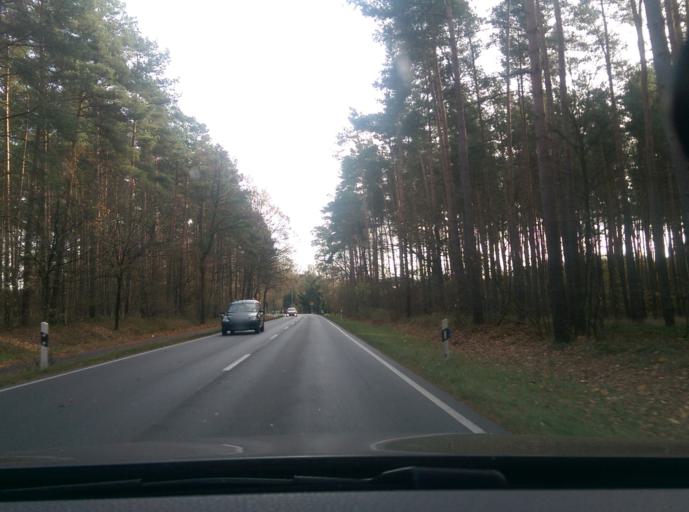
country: DE
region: Lower Saxony
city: Hambuhren
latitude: 52.6433
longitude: 10.0202
